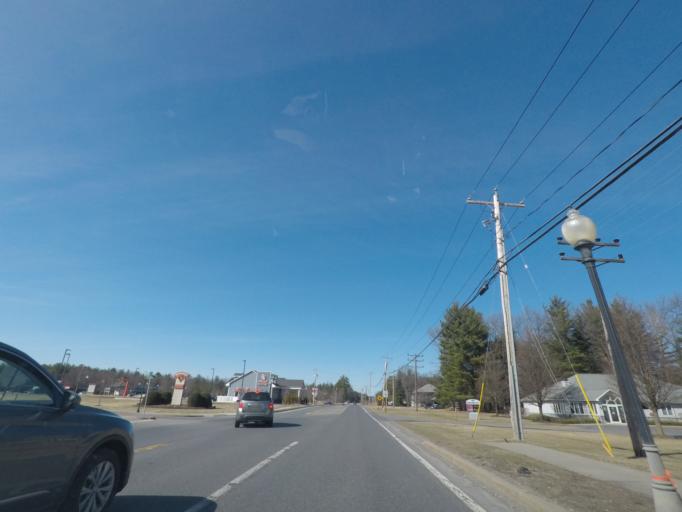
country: US
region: New York
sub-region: Saratoga County
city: Milton
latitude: 43.0472
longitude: -73.8504
